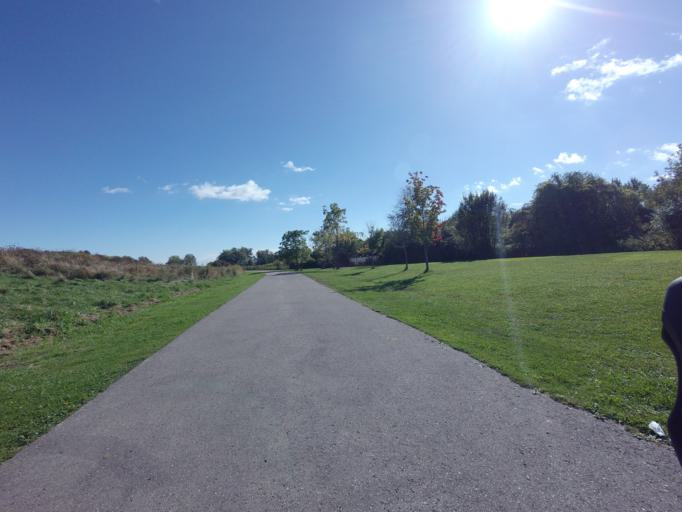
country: CA
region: Ontario
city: Ajax
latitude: 43.8486
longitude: -78.9499
